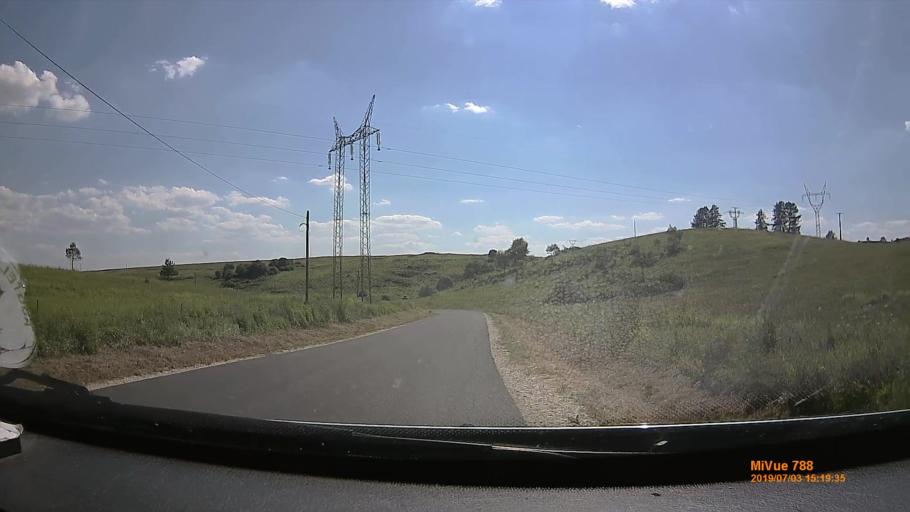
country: HU
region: Borsod-Abauj-Zemplen
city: Farkaslyuk
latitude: 48.2006
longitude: 20.3889
